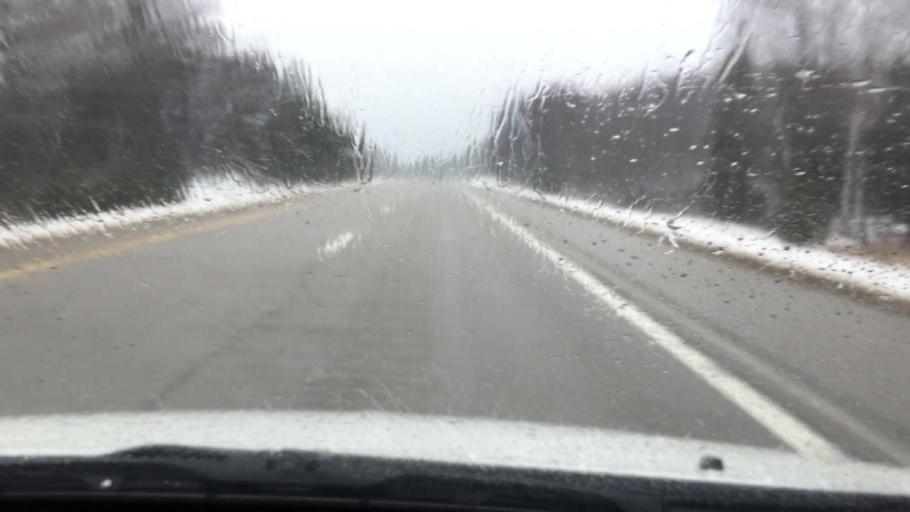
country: US
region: Michigan
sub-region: Wexford County
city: Cadillac
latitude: 44.1516
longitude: -85.4597
